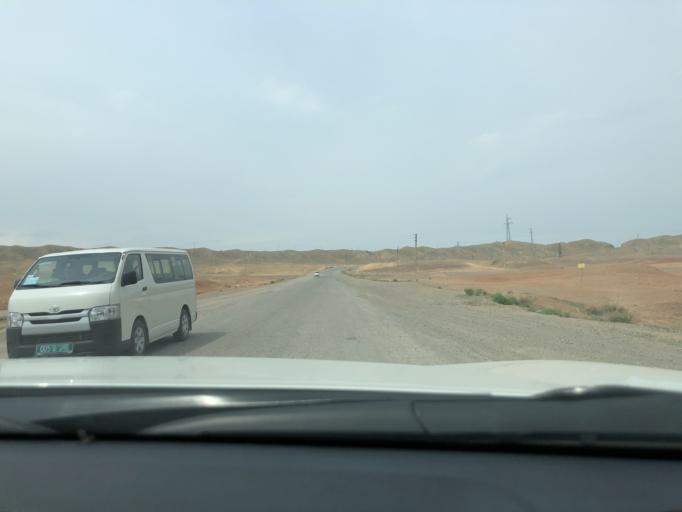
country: TJ
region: Viloyati Sughd
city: Kim
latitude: 40.2104
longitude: 70.4748
